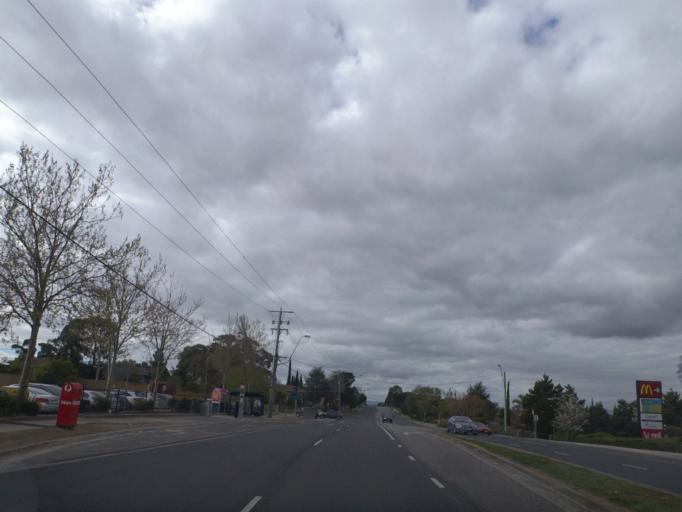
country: AU
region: Victoria
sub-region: Manningham
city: Templestowe Lower
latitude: -37.7735
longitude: 145.1144
